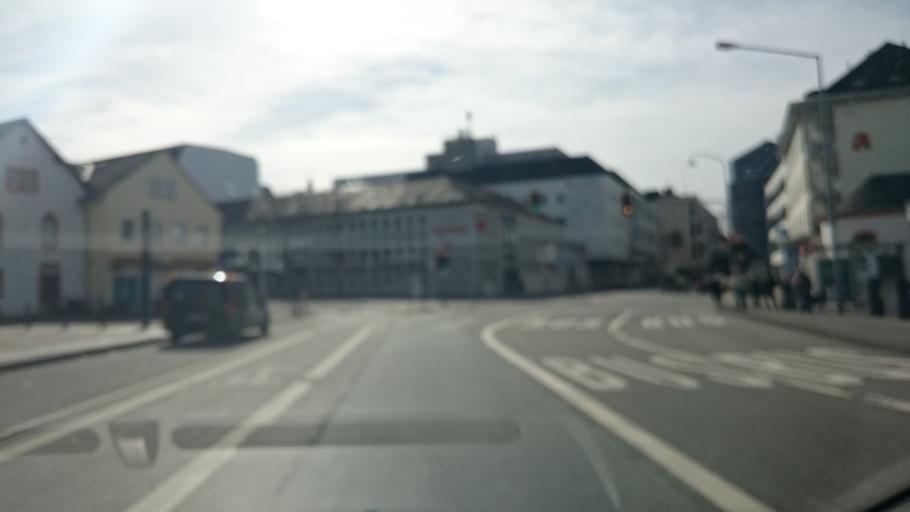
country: DE
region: Rheinland-Pfalz
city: Trier
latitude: 49.7598
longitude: 6.6425
